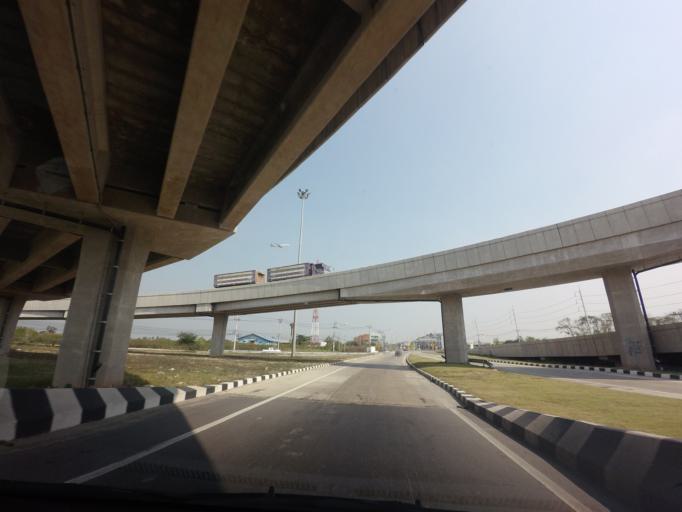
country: TH
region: Bangkok
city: Lat Krabang
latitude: 13.7563
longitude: 100.7485
